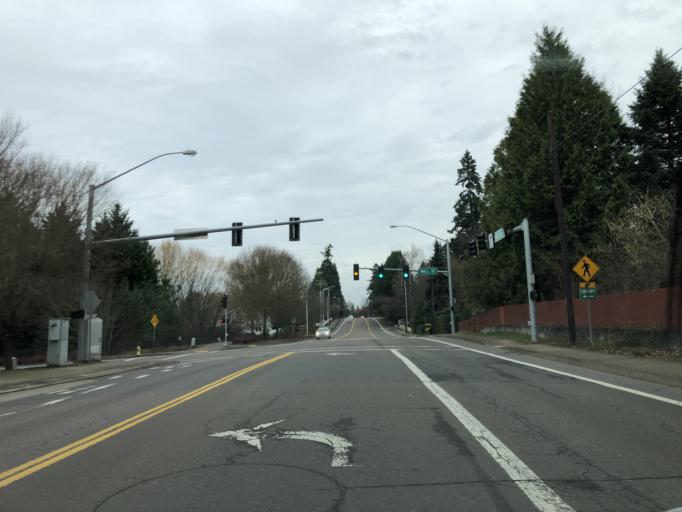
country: US
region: Oregon
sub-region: Washington County
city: Tigard
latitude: 45.4221
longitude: -122.7657
